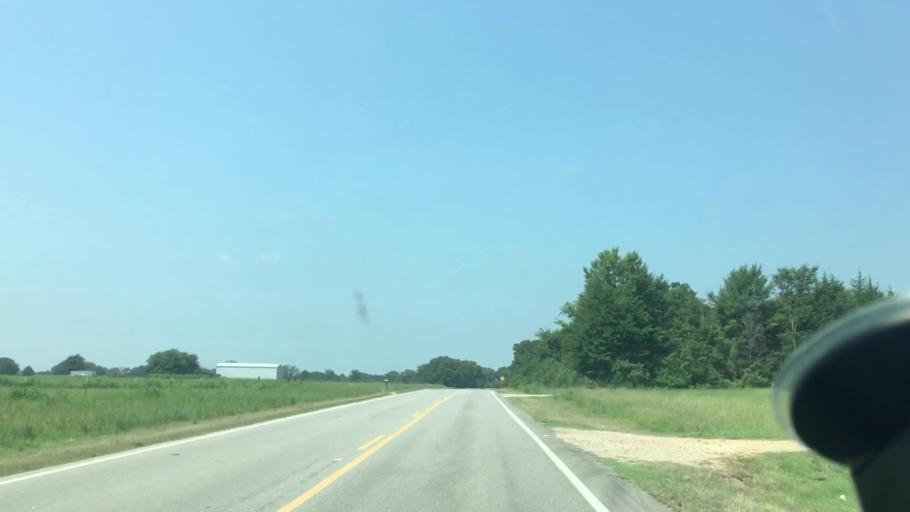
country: US
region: Oklahoma
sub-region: Atoka County
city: Atoka
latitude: 34.2795
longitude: -95.9438
